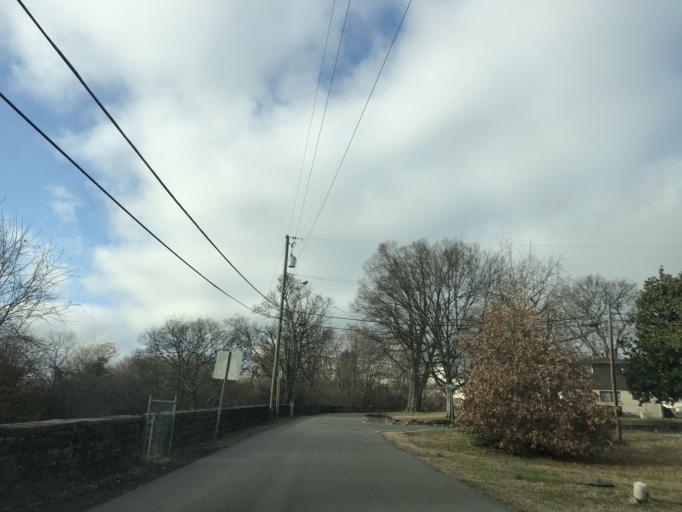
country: US
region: Tennessee
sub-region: Davidson County
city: Nashville
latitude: 36.1996
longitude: -86.7872
